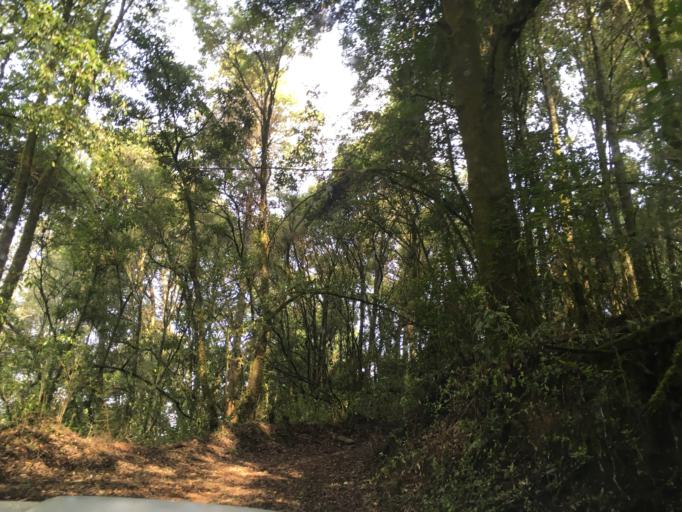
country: MX
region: Michoacan
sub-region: Zitacuaro
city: Francisco Serrato (San Bartolo)
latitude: 19.5120
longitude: -100.3027
